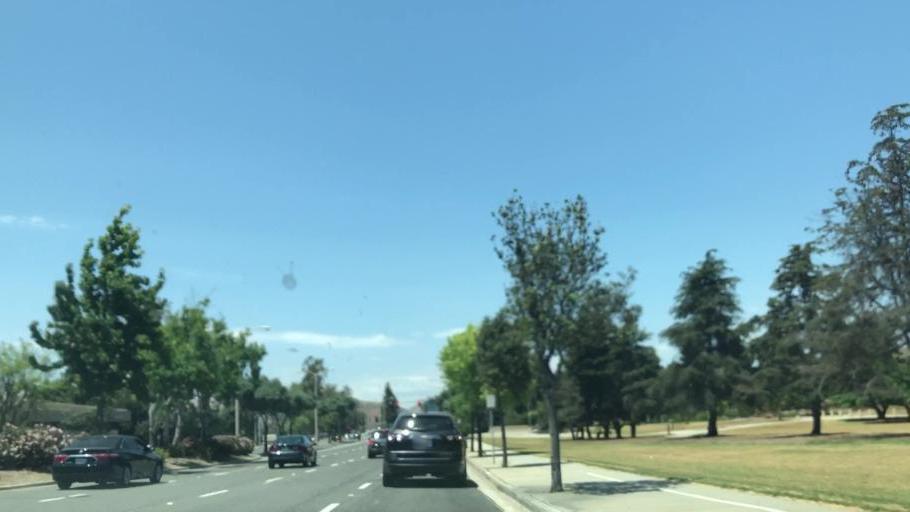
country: US
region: California
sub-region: Ventura County
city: El Rio
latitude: 34.2667
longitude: -119.2126
